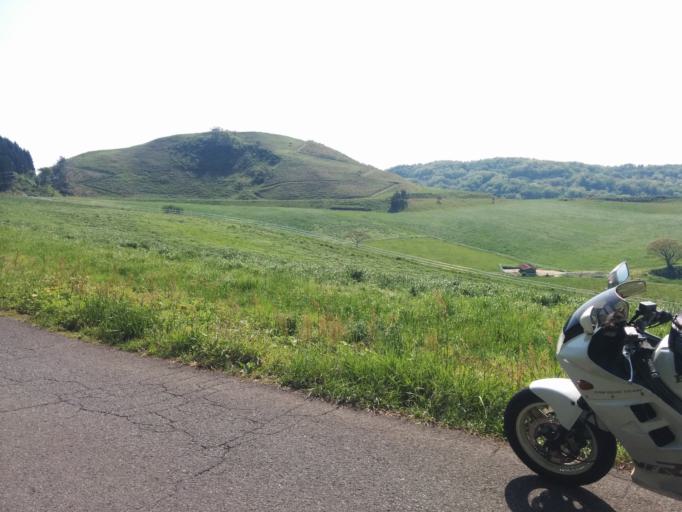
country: JP
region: Kyoto
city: Miyazu
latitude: 35.7277
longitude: 135.1986
